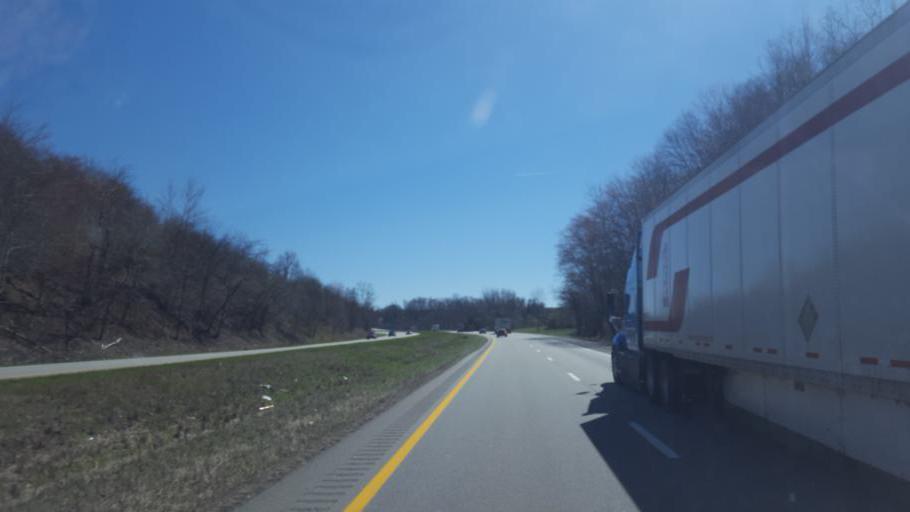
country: US
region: Ohio
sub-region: Belmont County
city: Barnesville
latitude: 40.0569
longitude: -81.2514
